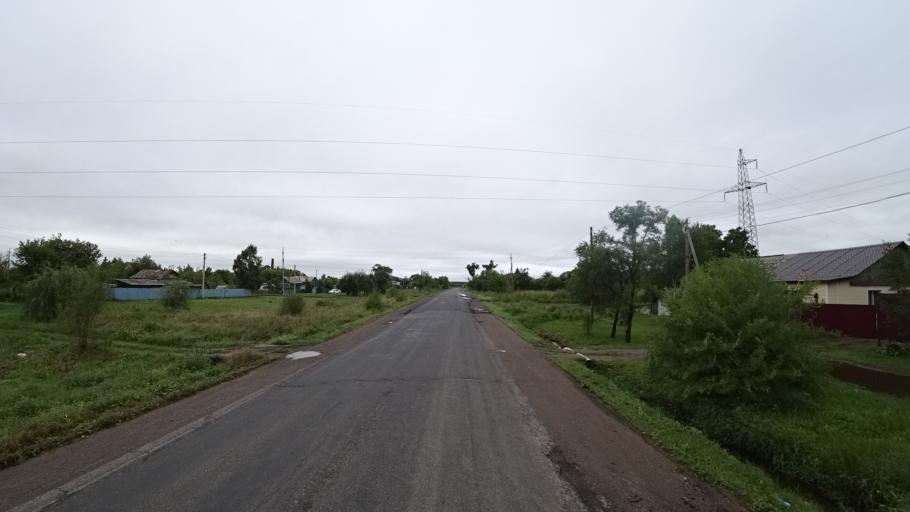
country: RU
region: Primorskiy
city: Monastyrishche
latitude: 44.2003
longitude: 132.4766
